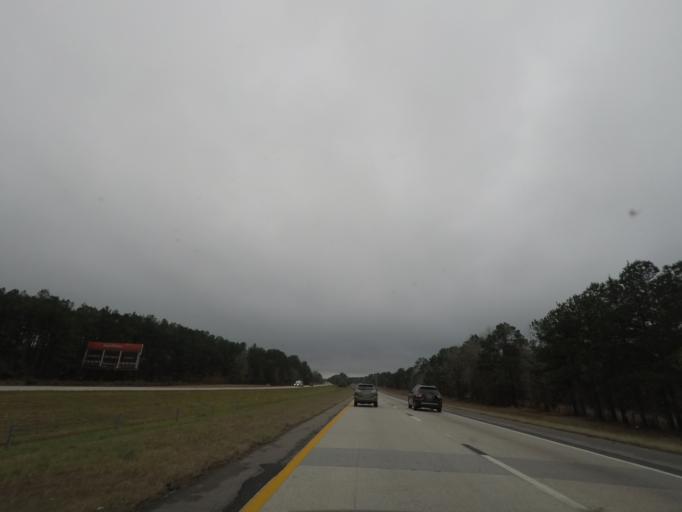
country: US
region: South Carolina
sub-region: Dorchester County
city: Saint George
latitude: 33.1712
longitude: -80.6168
